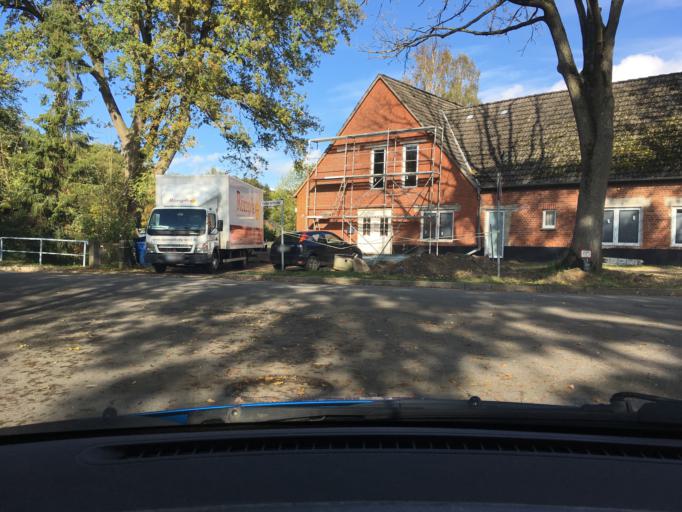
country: DE
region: Lower Saxony
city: Kakenstorf
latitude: 53.3183
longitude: 9.7940
